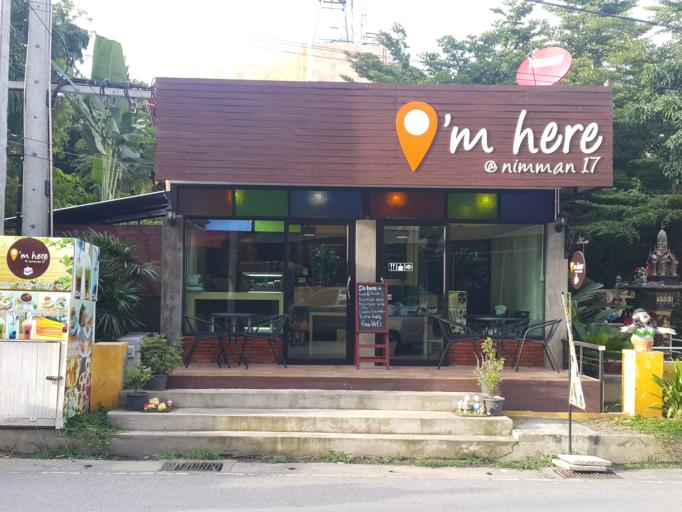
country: TH
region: Chiang Mai
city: Chiang Mai
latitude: 18.7948
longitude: 98.9692
